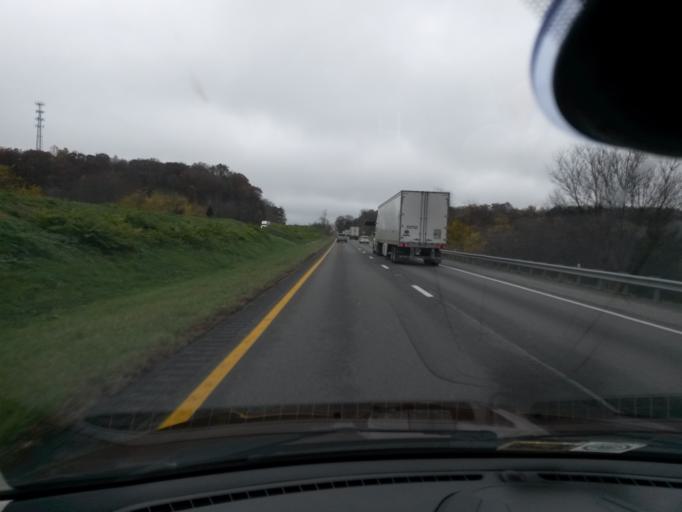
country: US
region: Virginia
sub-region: Carroll County
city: Woodlawn
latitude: 36.8939
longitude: -80.8752
